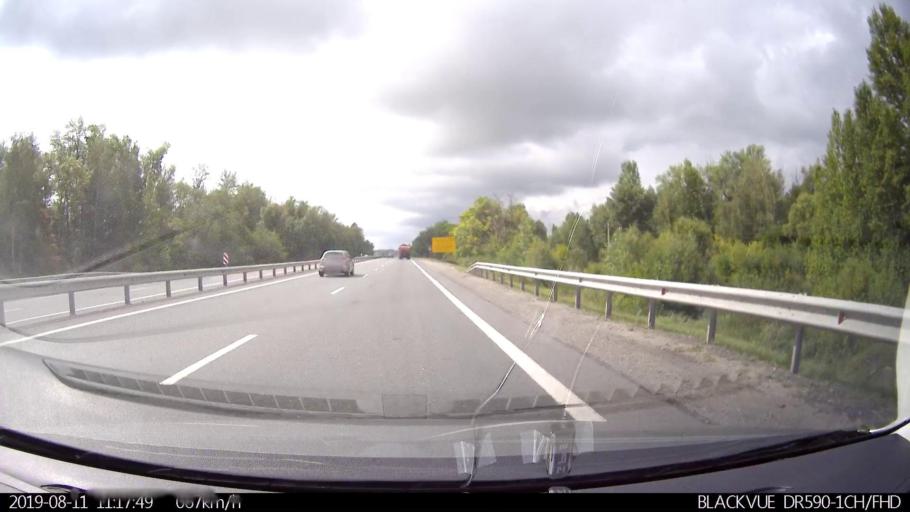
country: RU
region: Ulyanovsk
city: Novoul'yanovsk
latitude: 54.1854
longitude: 48.2735
